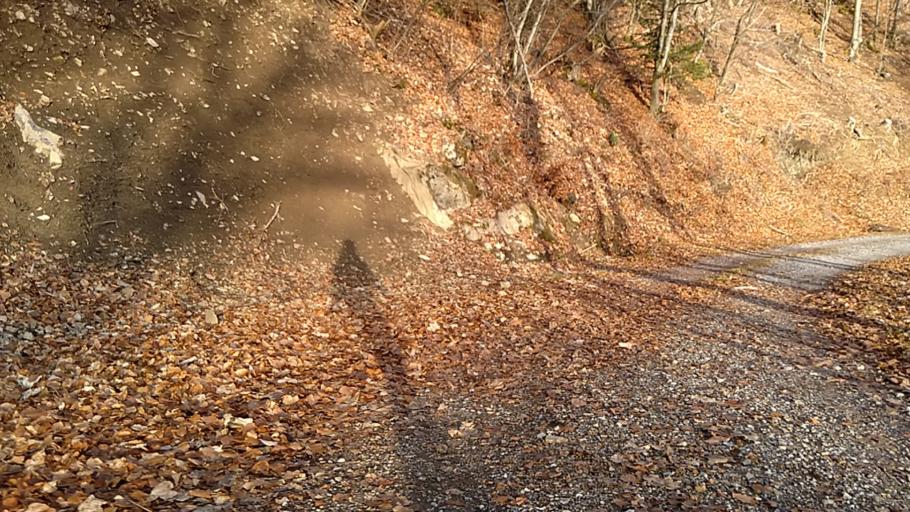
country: CH
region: Valais
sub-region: Monthey District
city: Vouvry
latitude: 46.3246
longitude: 6.8739
